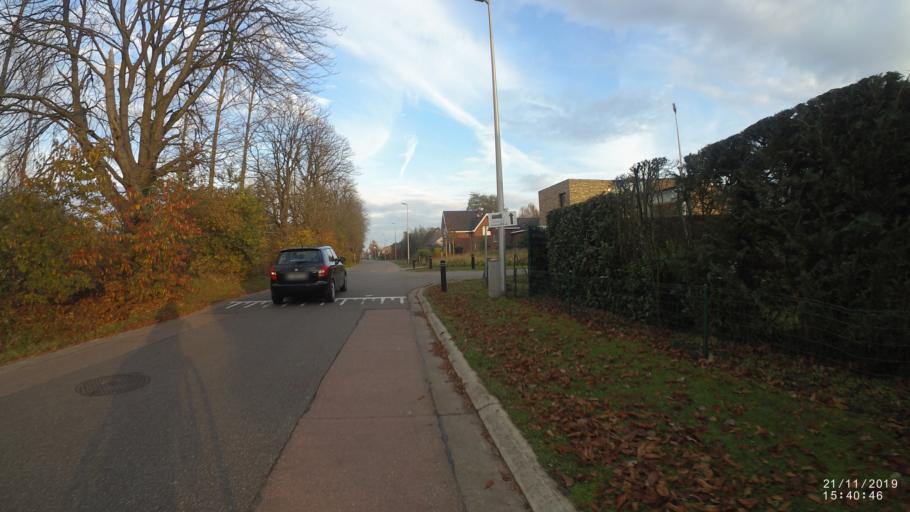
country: BE
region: Flanders
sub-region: Provincie Limburg
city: Hasselt
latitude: 50.9615
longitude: 5.3337
